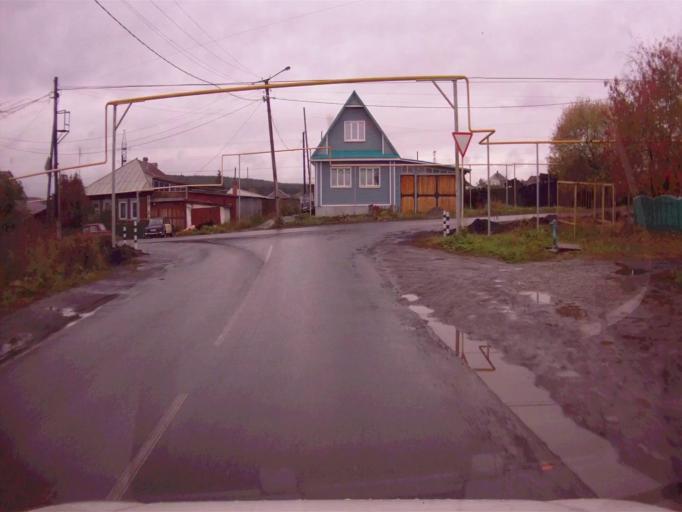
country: RU
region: Chelyabinsk
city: Verkhniy Ufaley
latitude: 56.0479
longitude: 60.2084
